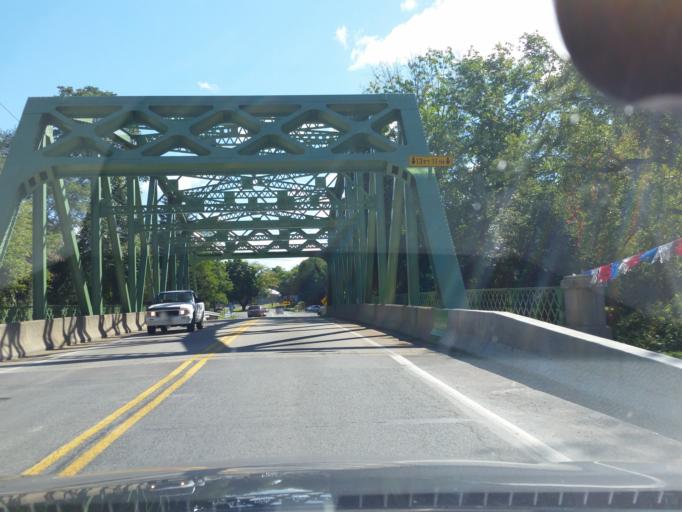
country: US
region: Pennsylvania
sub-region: Northumberland County
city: Sunbury
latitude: 40.8591
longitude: -76.7761
